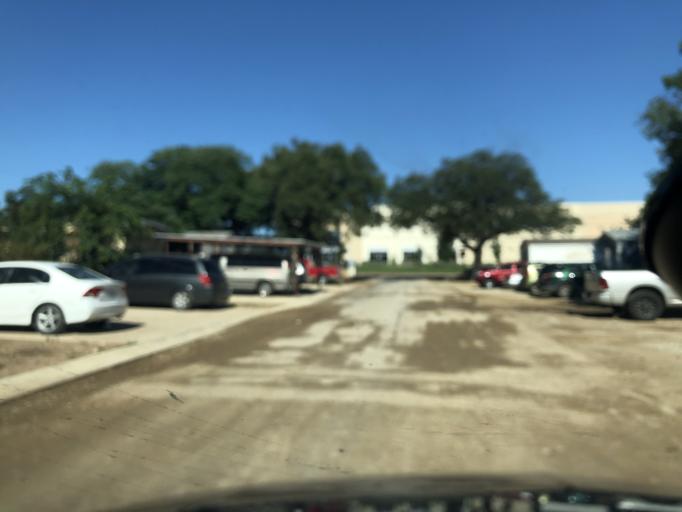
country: US
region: Texas
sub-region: Tarrant County
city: Euless
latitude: 32.8228
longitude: -97.0295
